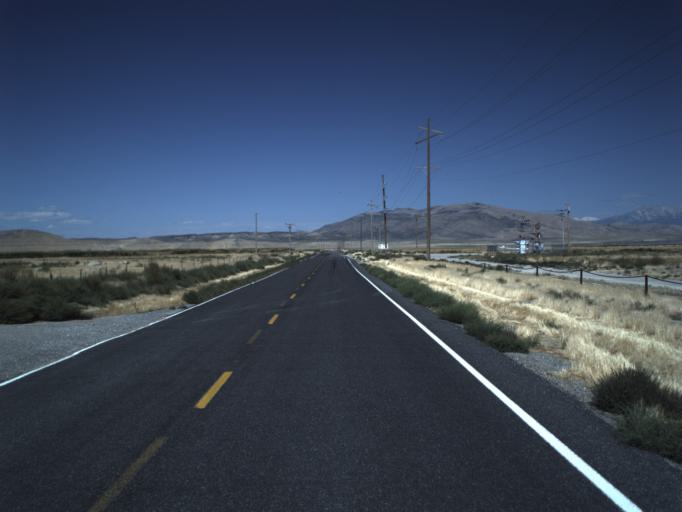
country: US
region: Utah
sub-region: Utah County
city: Genola
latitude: 40.0739
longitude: -111.9586
